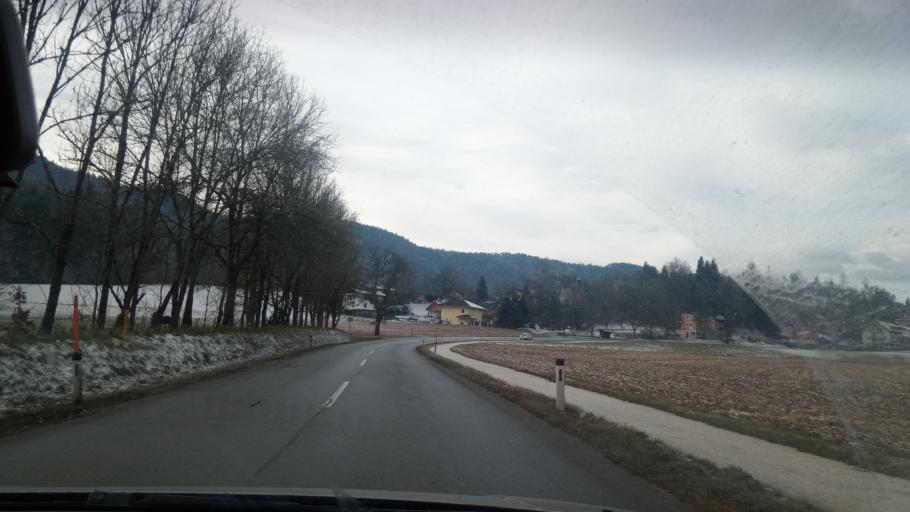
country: AT
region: Carinthia
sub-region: Politischer Bezirk Klagenfurt Land
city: Kottmannsdorf
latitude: 46.5882
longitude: 14.2413
